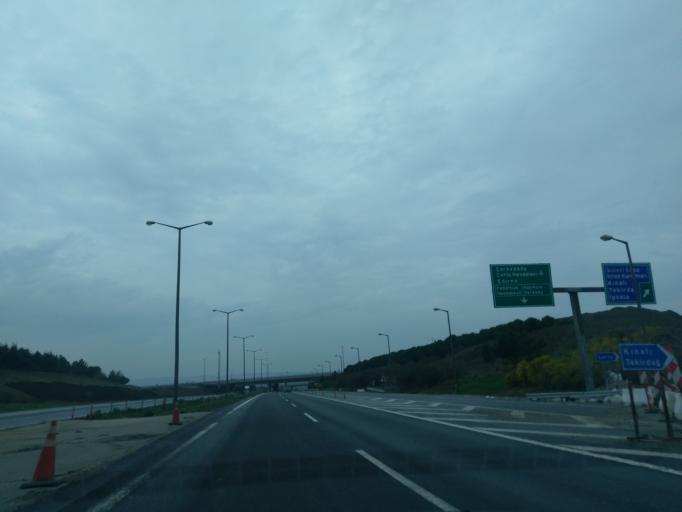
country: TR
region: Istanbul
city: Silivri
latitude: 41.1185
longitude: 28.1882
